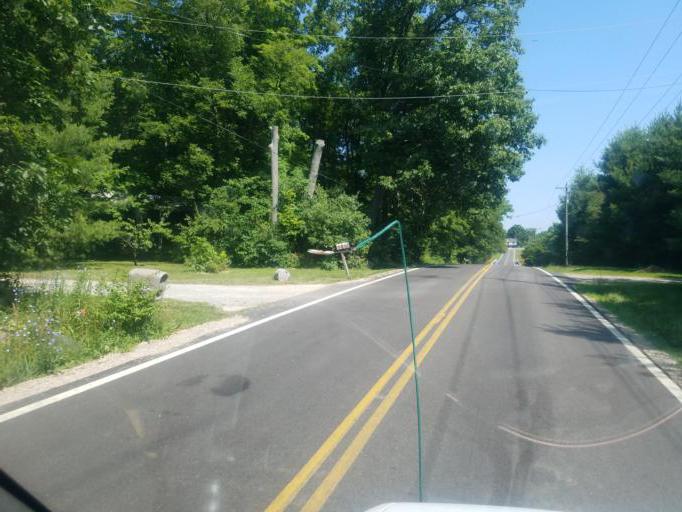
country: US
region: Ohio
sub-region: Union County
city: Marysville
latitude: 40.2211
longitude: -83.4551
